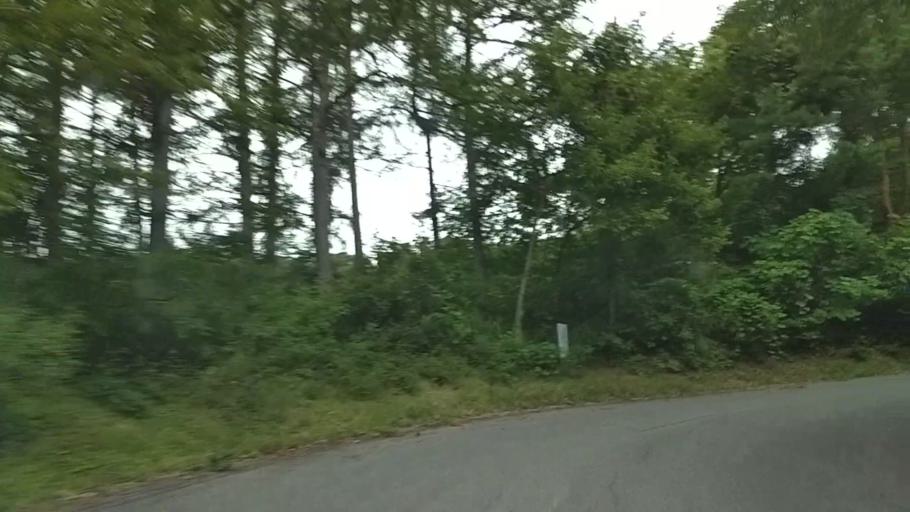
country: JP
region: Nagano
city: Iiyama
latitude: 36.8182
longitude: 138.3722
